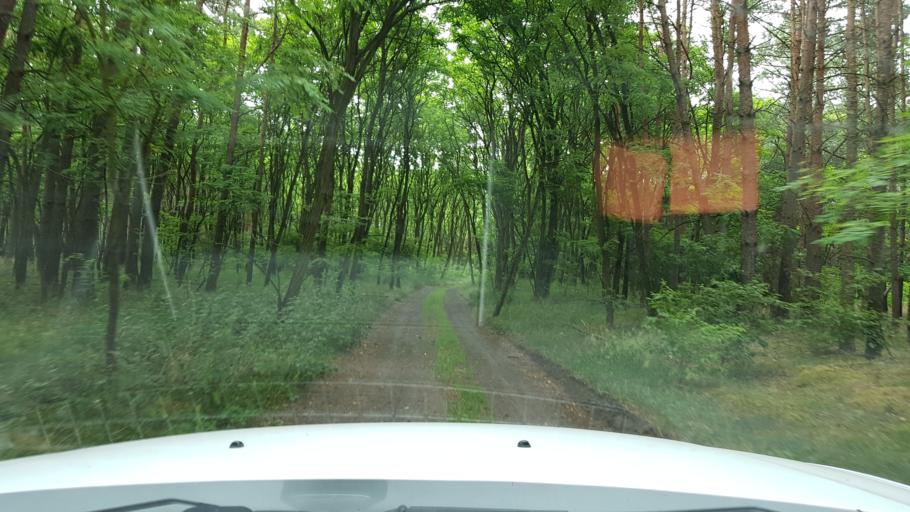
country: PL
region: West Pomeranian Voivodeship
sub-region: Powiat mysliborski
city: Boleszkowice
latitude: 52.6413
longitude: 14.5515
